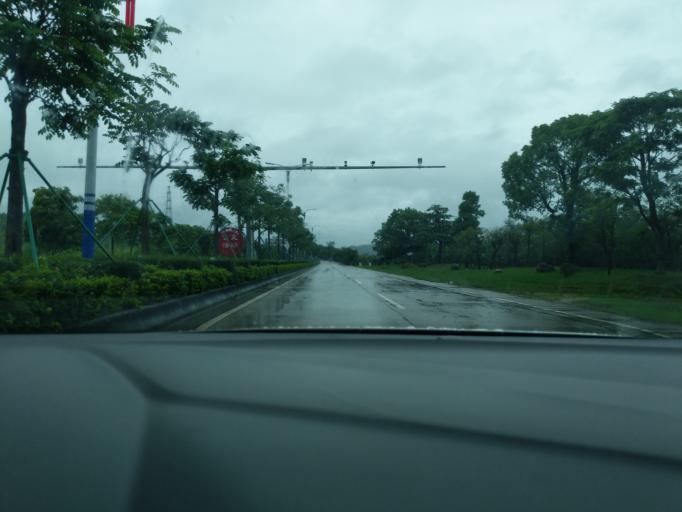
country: CN
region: Guangdong
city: Pingshi
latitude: 22.2208
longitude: 112.3170
